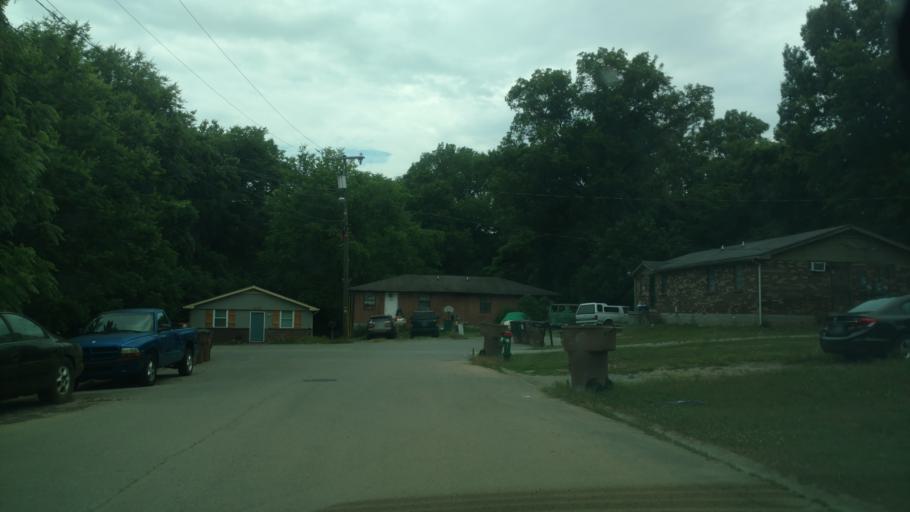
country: US
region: Tennessee
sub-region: Davidson County
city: Nashville
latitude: 36.1918
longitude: -86.7233
